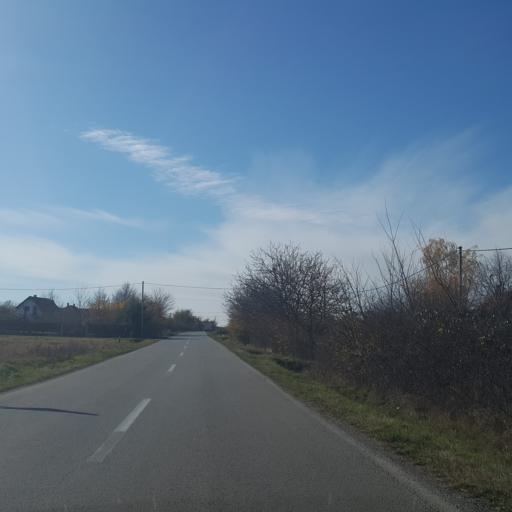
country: RS
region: Central Serbia
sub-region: Sumadijski Okrug
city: Topola
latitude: 44.2513
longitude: 20.7660
